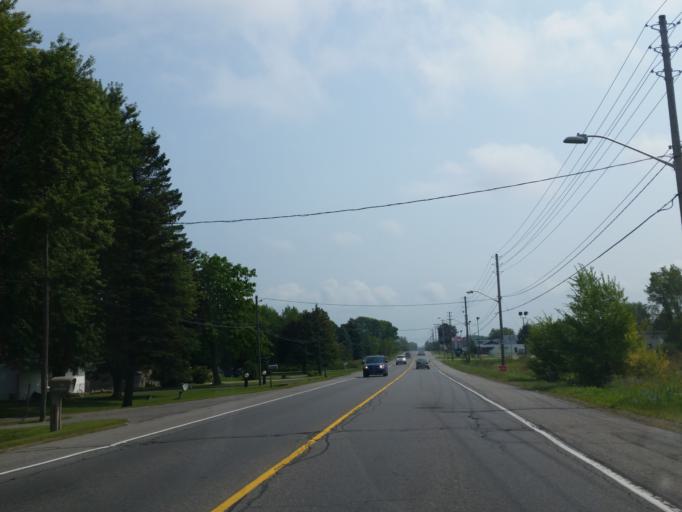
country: CA
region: Ontario
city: Brockville
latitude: 44.6075
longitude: -75.7251
